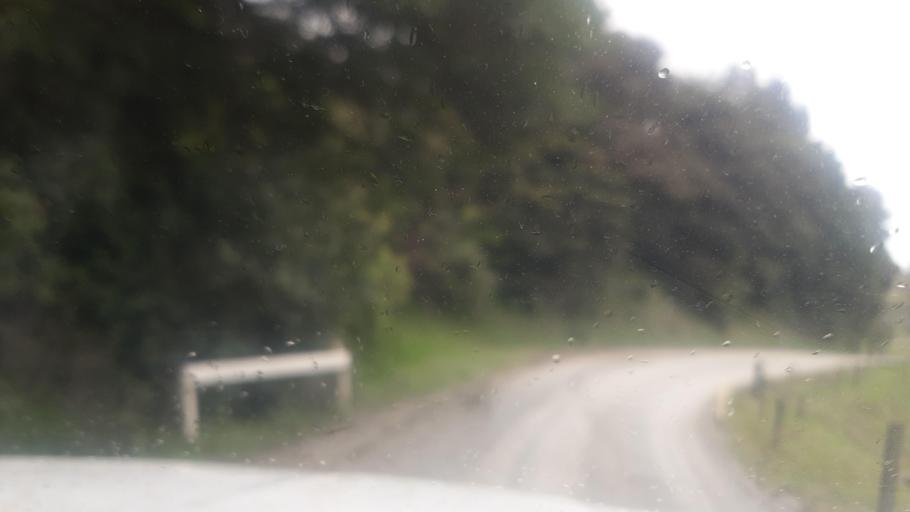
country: NZ
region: Northland
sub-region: Far North District
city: Taipa
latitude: -35.0997
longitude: 173.3987
